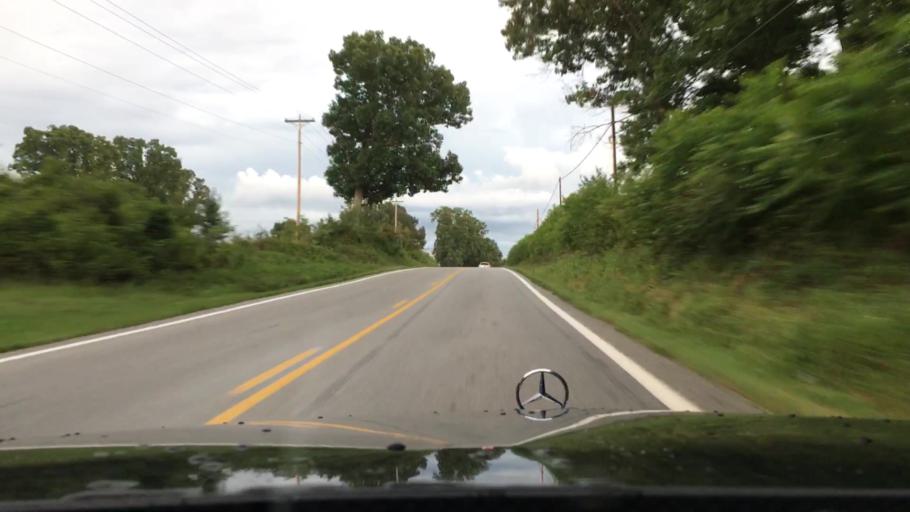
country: US
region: Virginia
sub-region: Amherst County
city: Amherst
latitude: 37.6299
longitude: -79.0188
